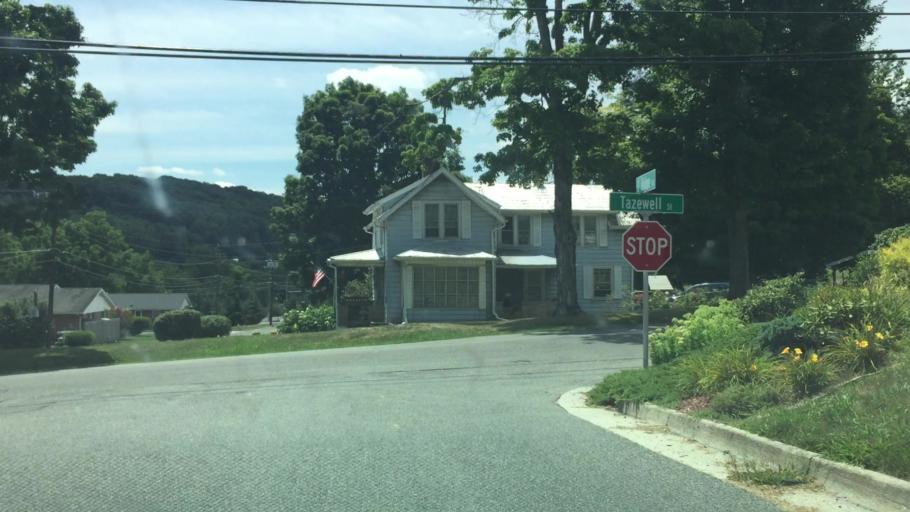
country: US
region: Virginia
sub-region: Wythe County
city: Wytheville
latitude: 36.9555
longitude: -81.0899
